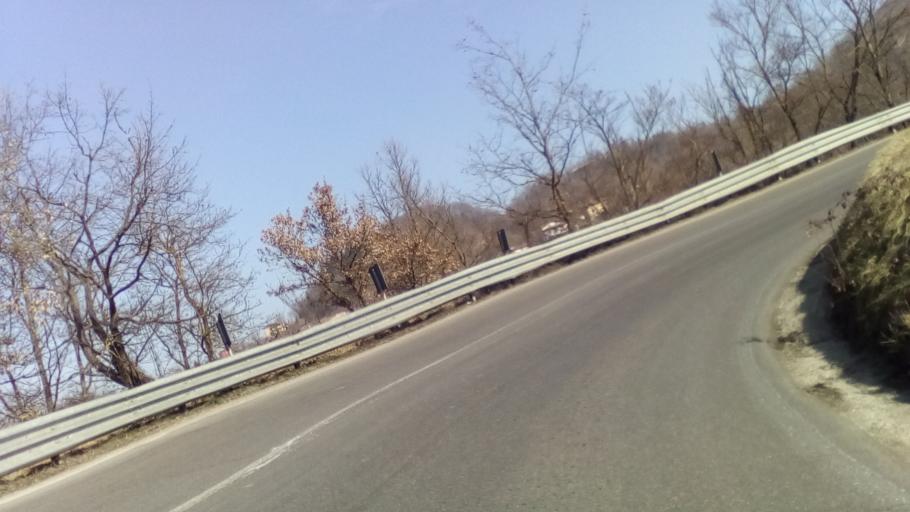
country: IT
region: Emilia-Romagna
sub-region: Provincia di Modena
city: Sant'Antonio
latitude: 44.3542
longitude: 10.8373
